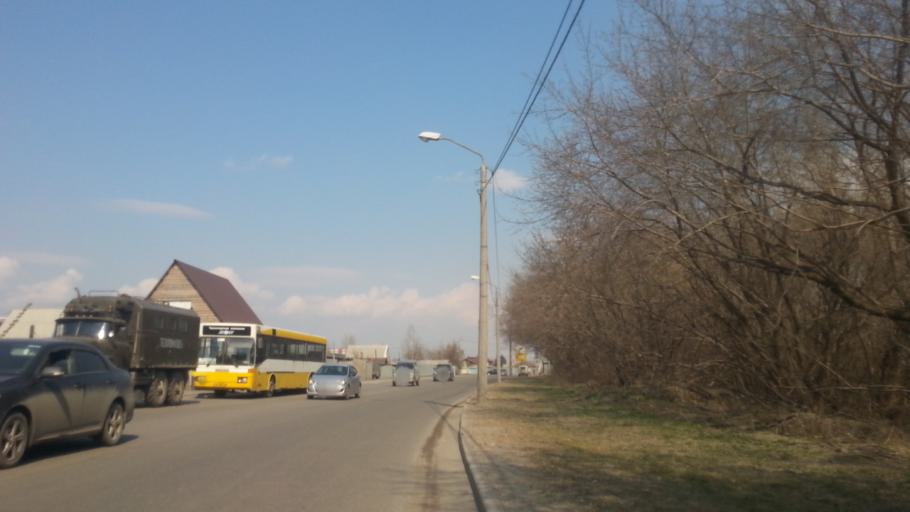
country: RU
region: Altai Krai
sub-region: Gorod Barnaulskiy
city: Barnaul
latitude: 53.3221
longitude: 83.7649
